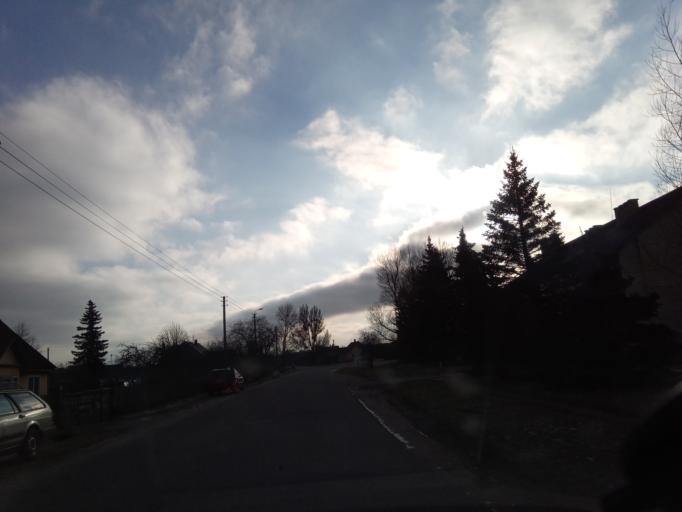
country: LT
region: Alytaus apskritis
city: Druskininkai
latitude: 53.9502
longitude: 24.2950
